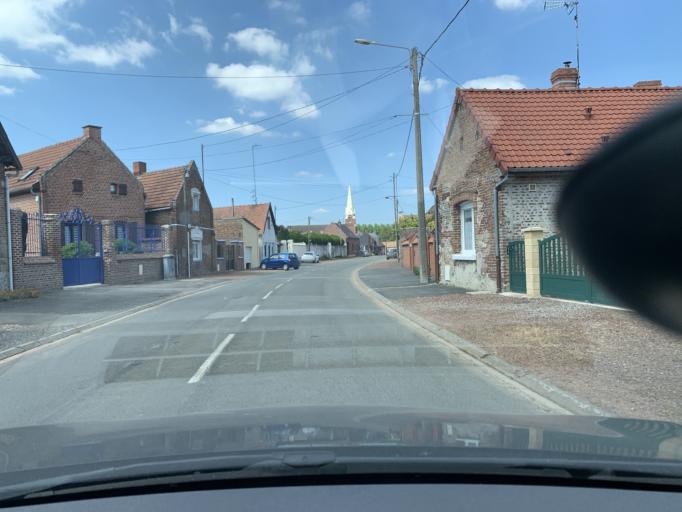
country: FR
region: Nord-Pas-de-Calais
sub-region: Departement du Pas-de-Calais
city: Marquion
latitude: 50.2343
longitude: 3.0968
